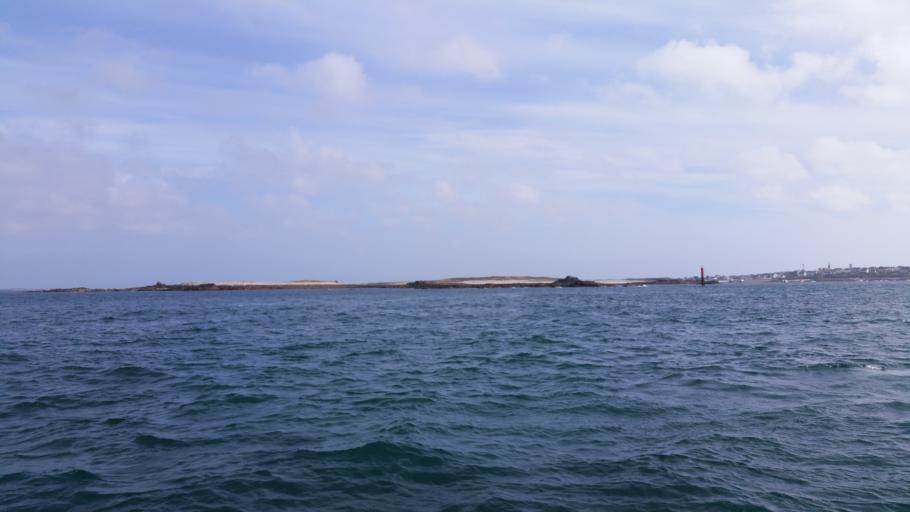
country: FR
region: Brittany
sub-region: Departement du Finistere
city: Le Conquet
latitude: 48.4123
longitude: -4.9496
